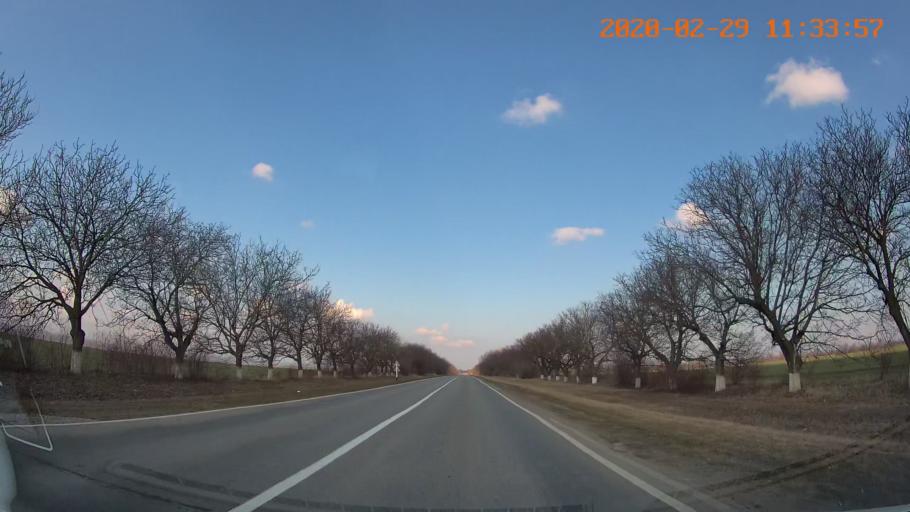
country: MD
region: Rezina
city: Saharna
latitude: 47.5587
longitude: 29.0790
